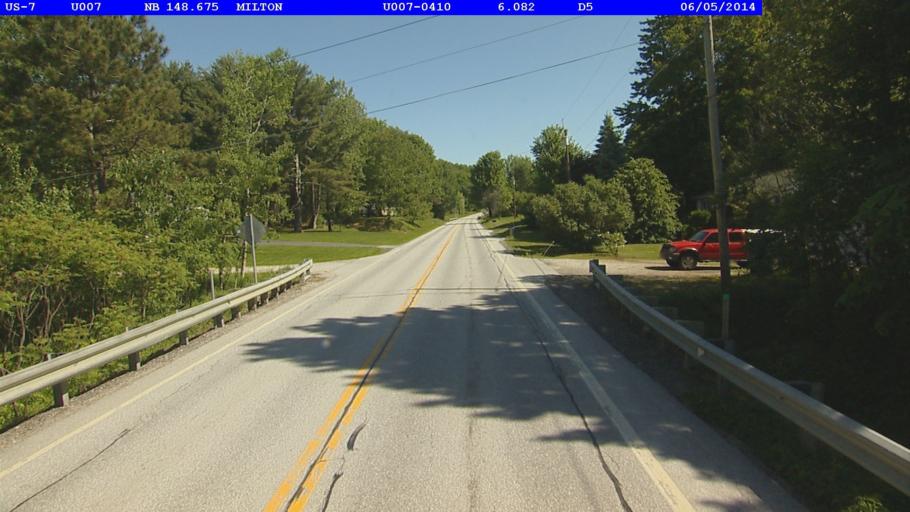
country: US
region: Vermont
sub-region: Chittenden County
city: Milton
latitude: 44.6543
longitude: -73.1141
